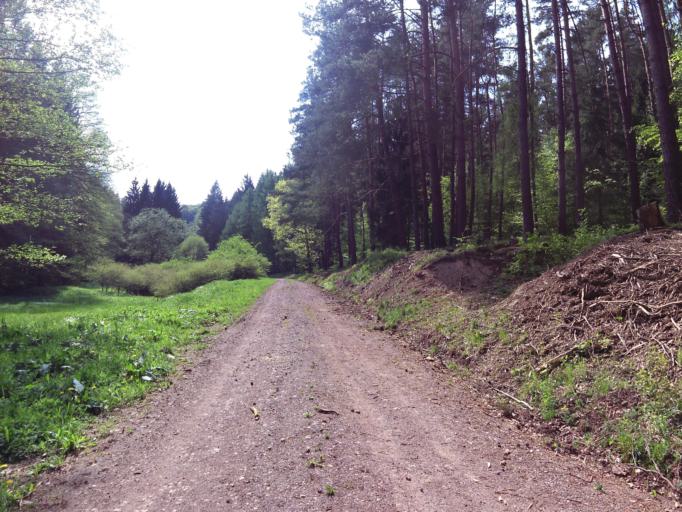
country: DE
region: Thuringia
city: Eisenach
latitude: 50.9620
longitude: 10.2903
